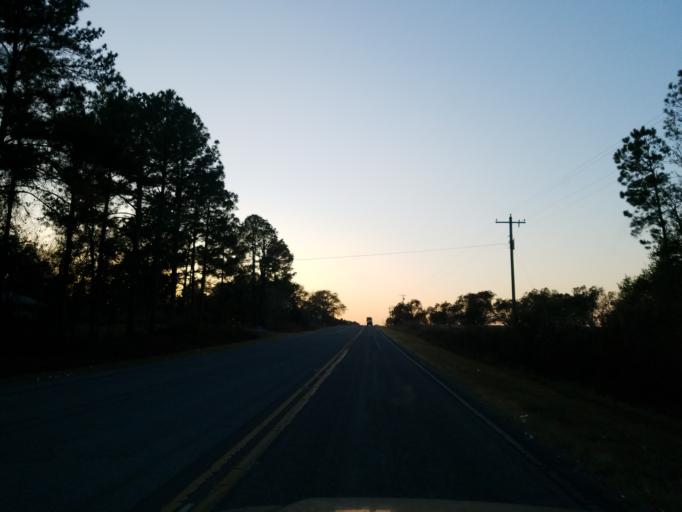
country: US
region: Georgia
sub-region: Ben Hill County
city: Fitzgerald
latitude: 31.7198
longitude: -83.3914
